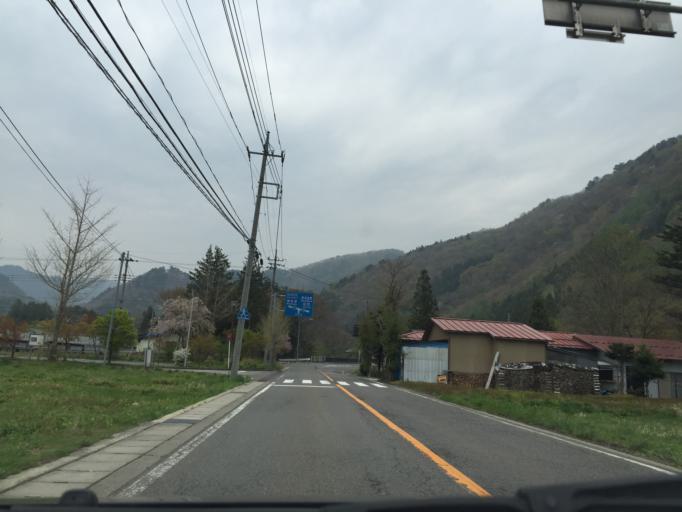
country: JP
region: Tochigi
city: Nikko
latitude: 37.0130
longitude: 139.7282
